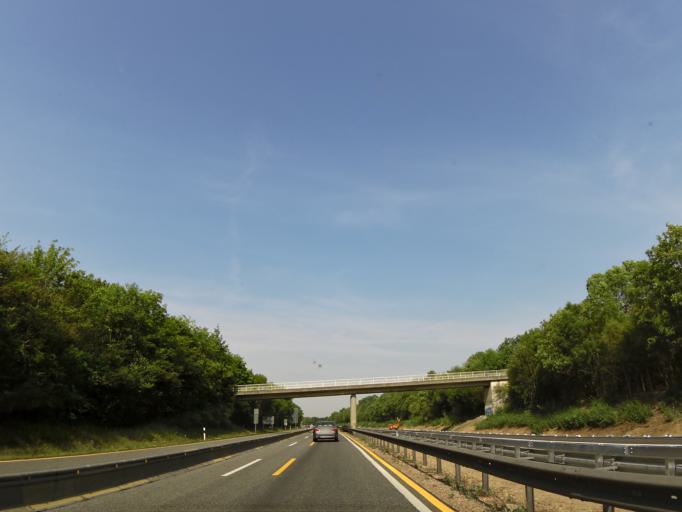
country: DE
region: Rheinland-Pfalz
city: Gundersheim
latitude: 49.7016
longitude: 8.1996
